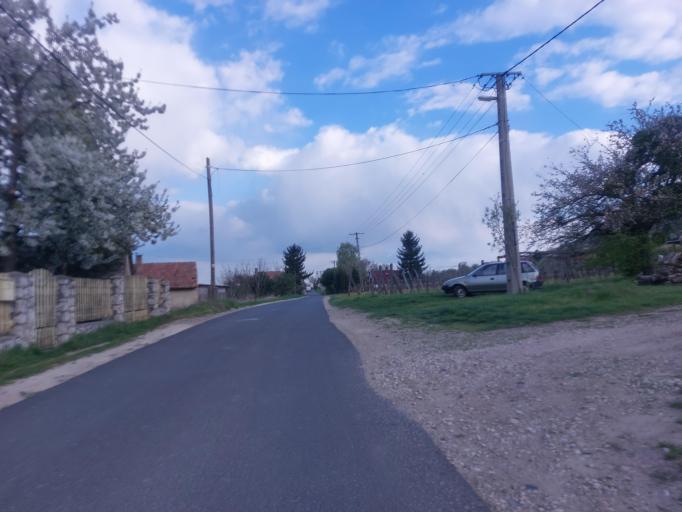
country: HU
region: Veszprem
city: Devecser
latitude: 47.1580
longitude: 17.3760
